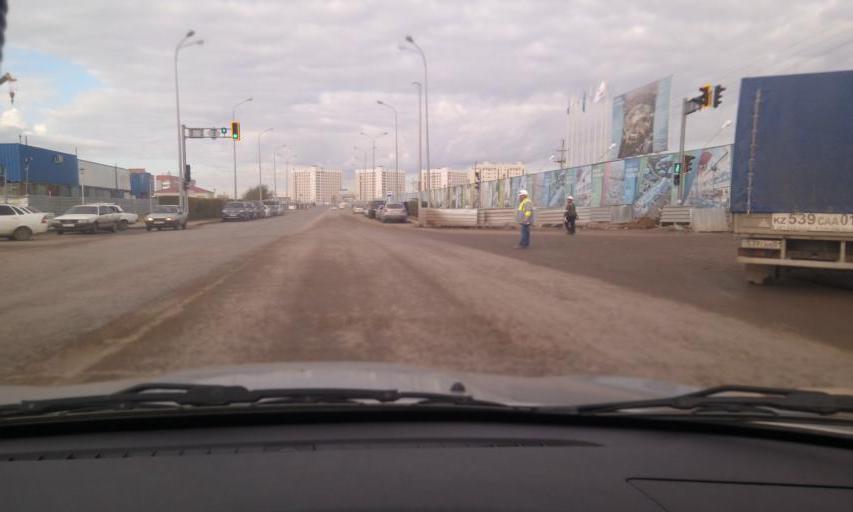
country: KZ
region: Astana Qalasy
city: Astana
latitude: 51.0856
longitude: 71.4076
